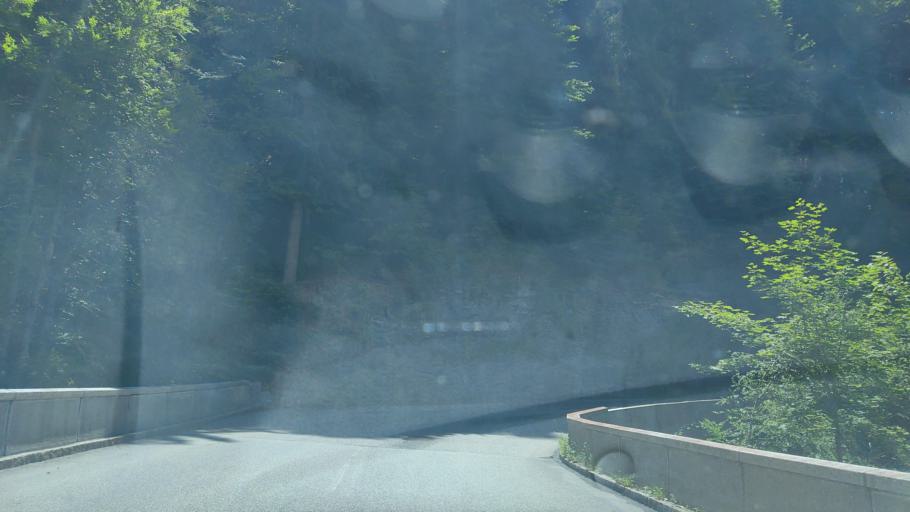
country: FR
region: Rhone-Alpes
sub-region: Departement de la Haute-Savoie
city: Praz-sur-Arly
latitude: 45.8331
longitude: 6.5089
